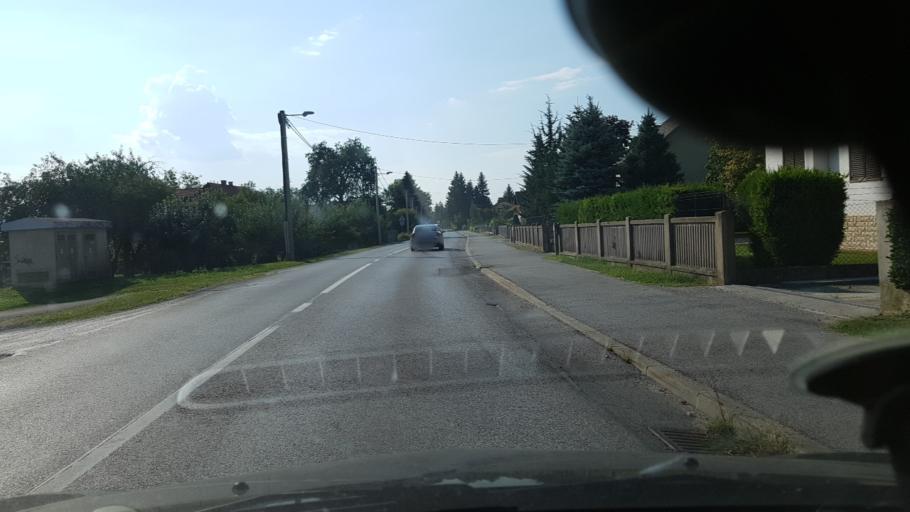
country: HR
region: Zagrebacka
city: Brdovec
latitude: 45.8678
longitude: 15.7592
